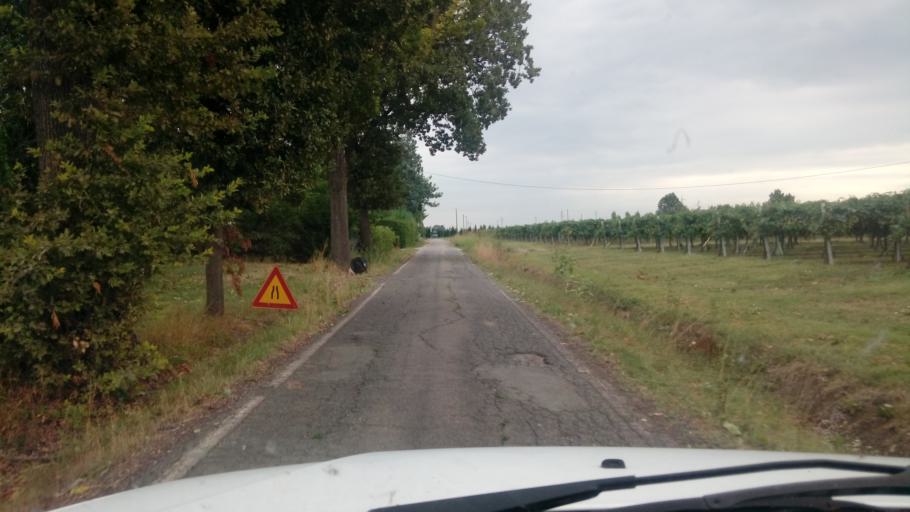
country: IT
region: Emilia-Romagna
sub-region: Provincia di Reggio Emilia
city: Fogliano
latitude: 44.6617
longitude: 10.6747
